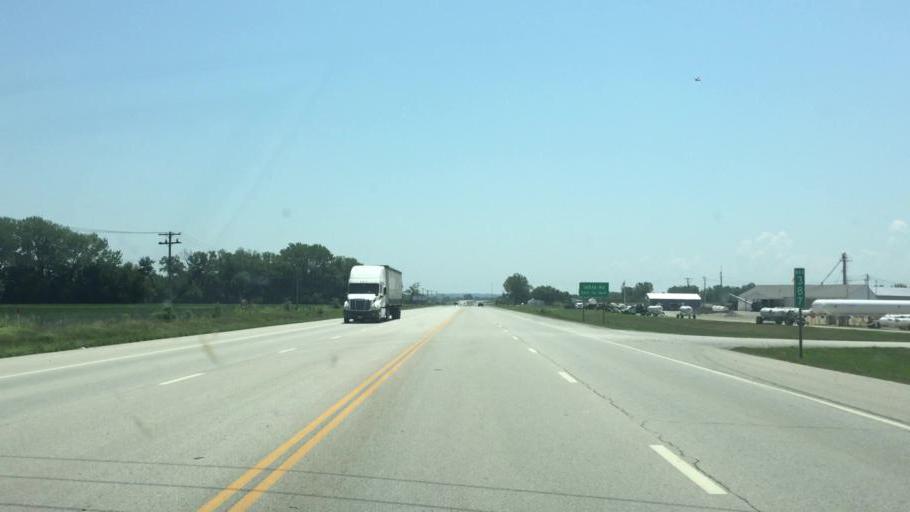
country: US
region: Kansas
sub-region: Doniphan County
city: Wathena
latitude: 39.7568
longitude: -94.9402
